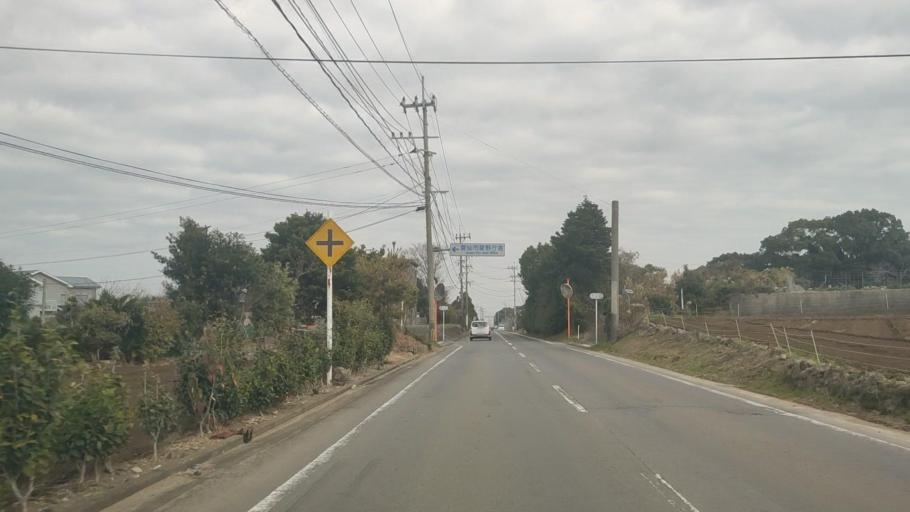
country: JP
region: Nagasaki
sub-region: Isahaya-shi
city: Isahaya
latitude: 32.8051
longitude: 130.1679
